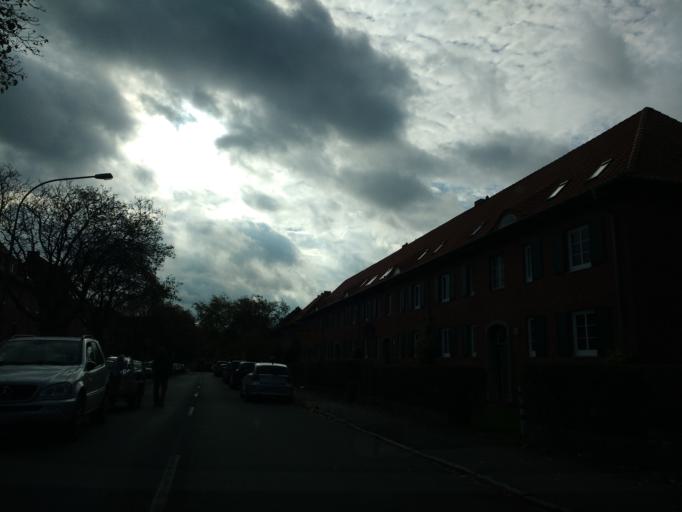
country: DE
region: Schleswig-Holstein
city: Travemuende
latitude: 53.9674
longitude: 10.8714
